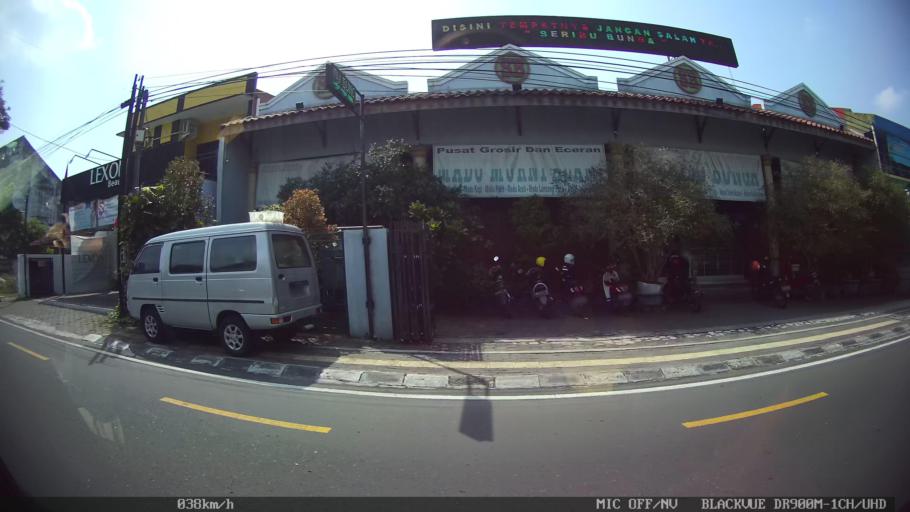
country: ID
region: Daerah Istimewa Yogyakarta
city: Yogyakarta
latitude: -7.8047
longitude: 110.3948
